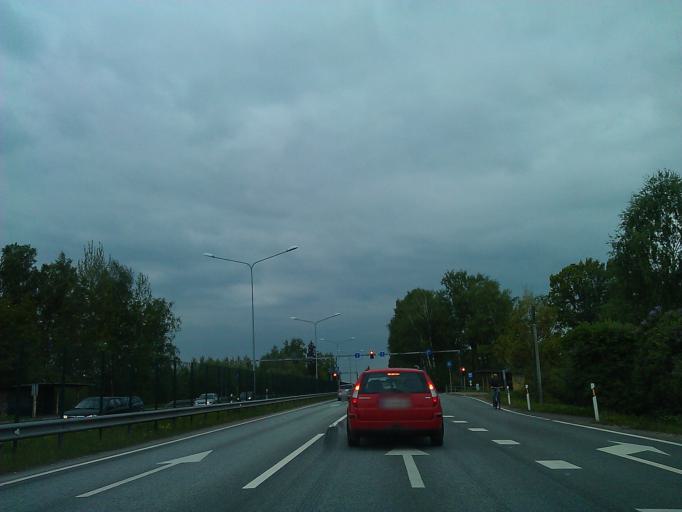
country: LV
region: Olaine
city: Olaine
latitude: 56.7845
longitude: 23.9505
